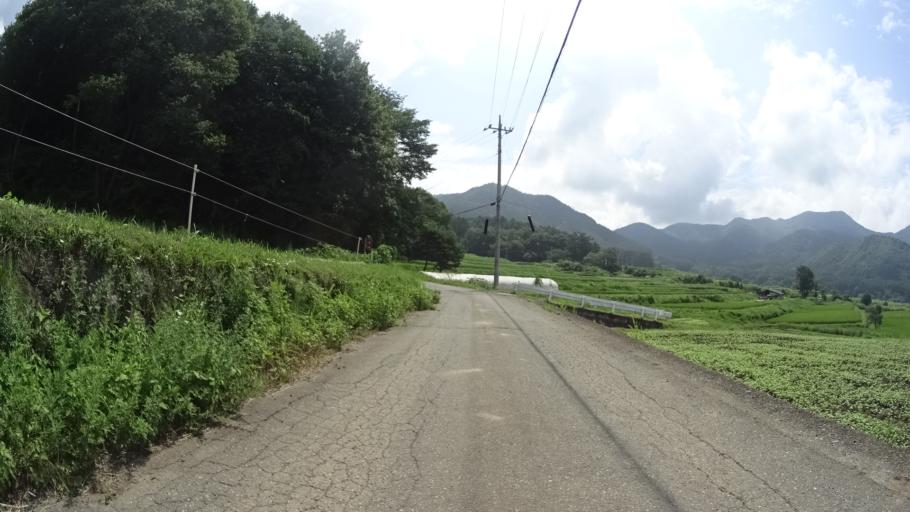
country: JP
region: Yamanashi
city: Nirasaki
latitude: 35.8930
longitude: 138.4710
